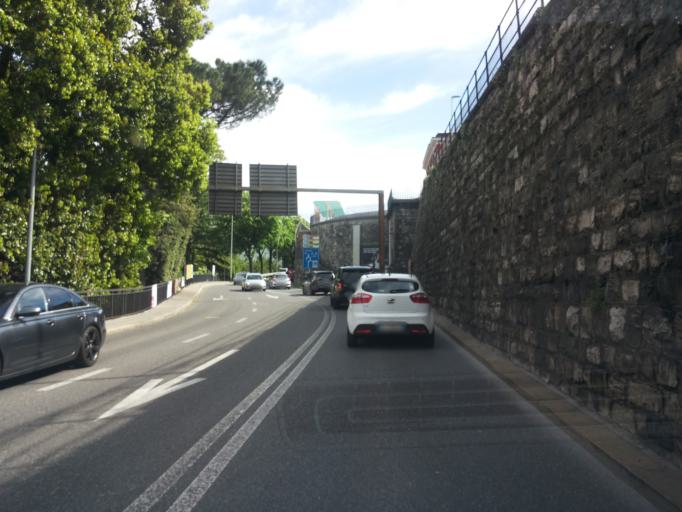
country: CH
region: Ticino
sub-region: Lugano District
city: Massagno
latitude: 46.0064
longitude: 8.9468
